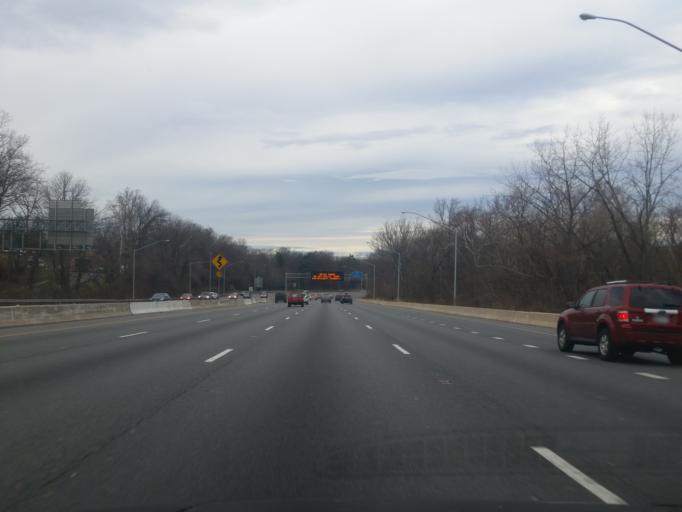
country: US
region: Maryland
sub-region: Montgomery County
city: South Kensington
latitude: 39.0063
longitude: -77.0842
